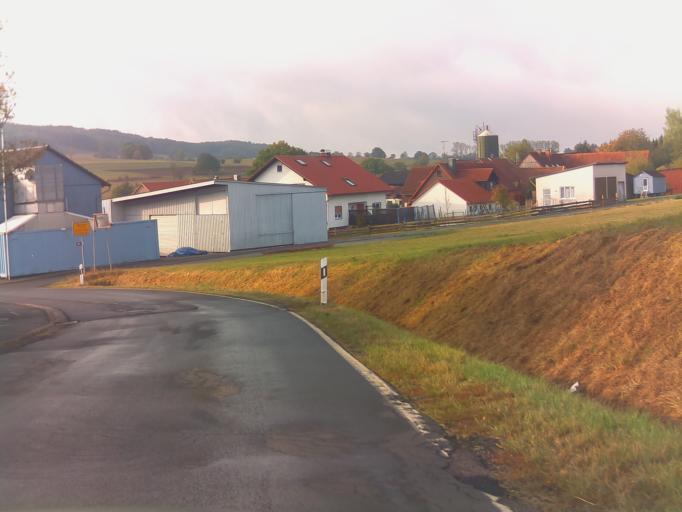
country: DE
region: Hesse
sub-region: Regierungsbezirk Giessen
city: Freiensteinau
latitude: 50.4850
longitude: 9.4002
